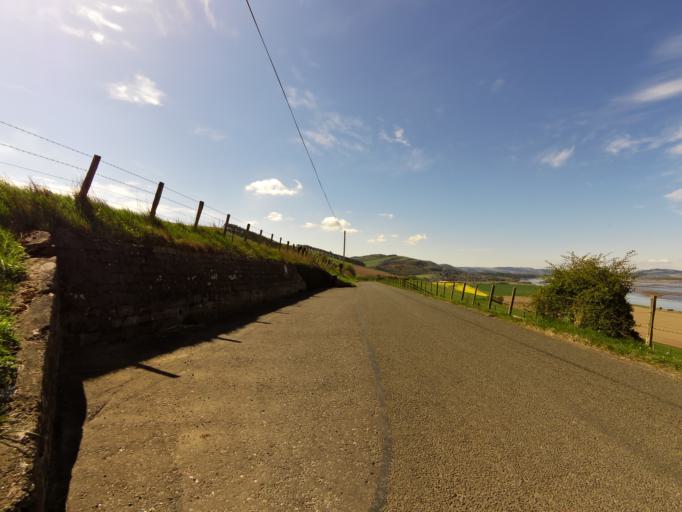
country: GB
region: Scotland
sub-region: Perth and Kinross
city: Errol
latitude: 56.3612
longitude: -3.1945
